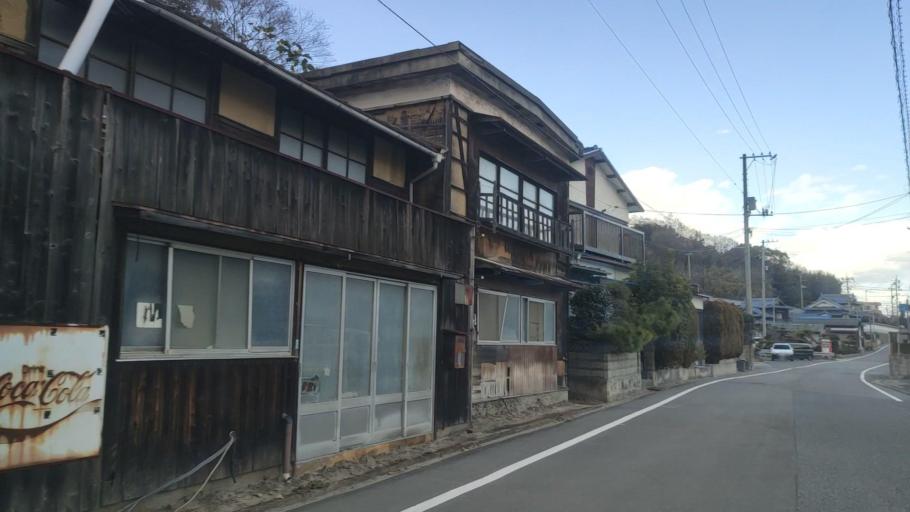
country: JP
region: Hiroshima
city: Innoshima
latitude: 34.1997
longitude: 133.1042
